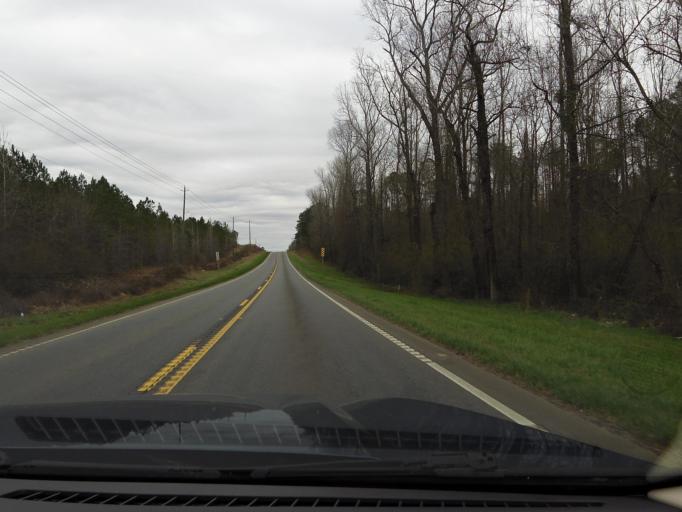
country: US
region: Georgia
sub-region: Randolph County
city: Cuthbert
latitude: 31.7744
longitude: -84.7508
